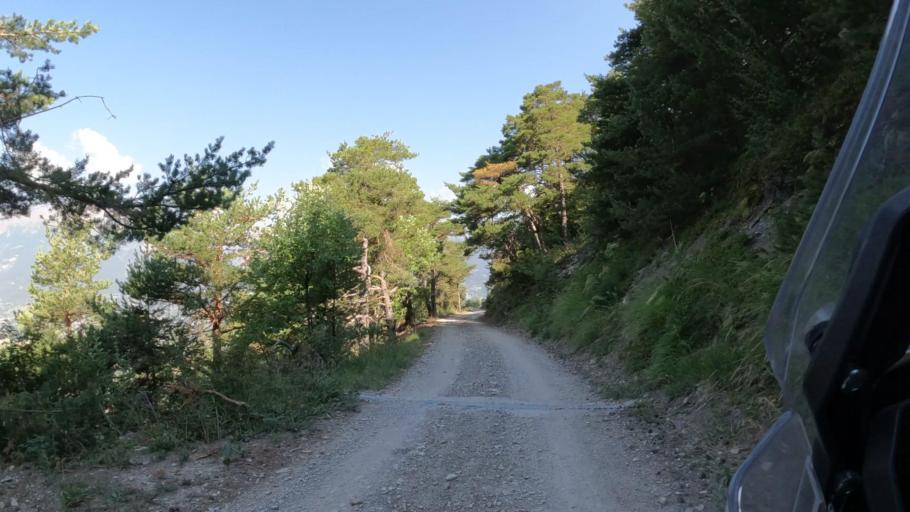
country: FR
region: Provence-Alpes-Cote d'Azur
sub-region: Departement des Hautes-Alpes
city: Embrun
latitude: 44.5972
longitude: 6.5644
